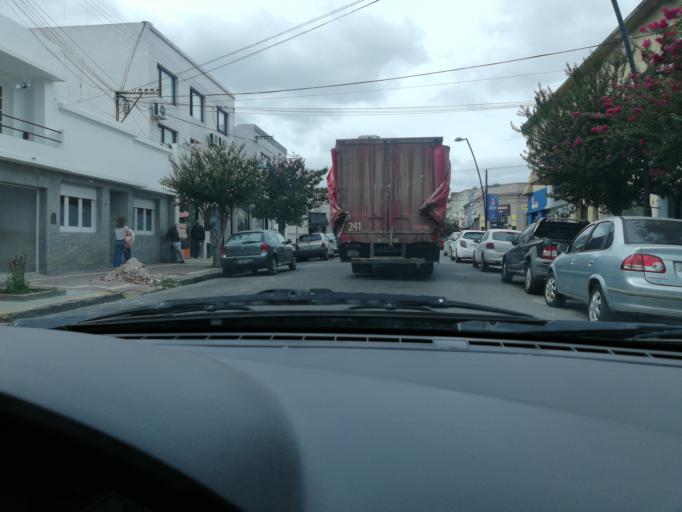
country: AR
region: Buenos Aires
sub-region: Partido de Balcarce
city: Balcarce
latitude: -37.8501
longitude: -58.2568
